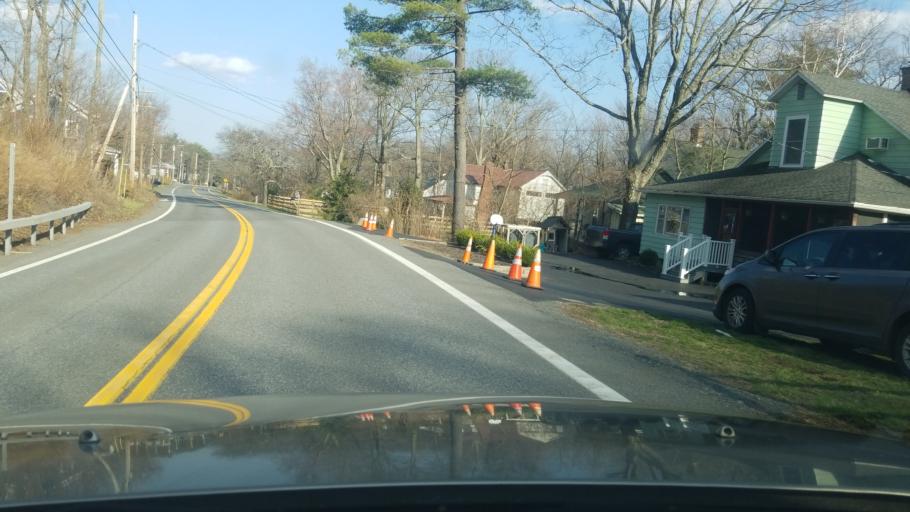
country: US
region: New York
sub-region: Greene County
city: Palenville
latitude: 42.1754
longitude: -74.0276
